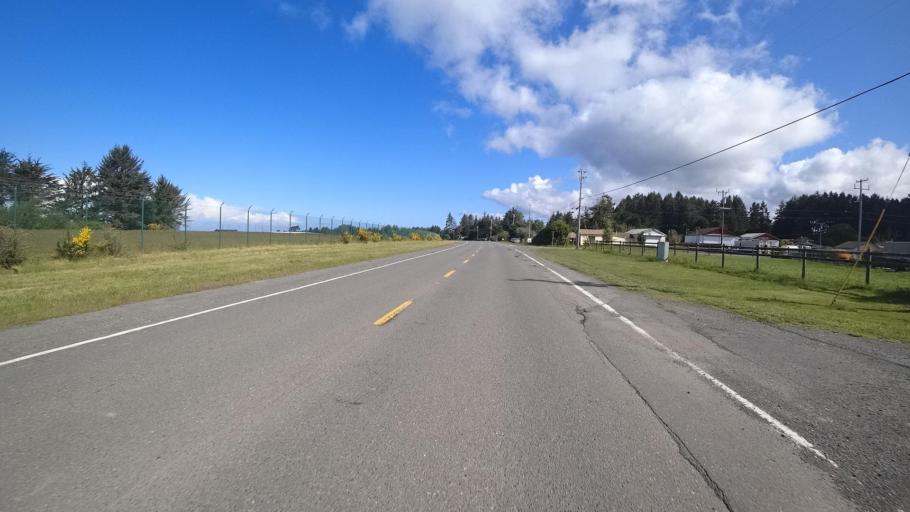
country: US
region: California
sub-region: Humboldt County
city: McKinleyville
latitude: 40.9791
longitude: -124.1008
